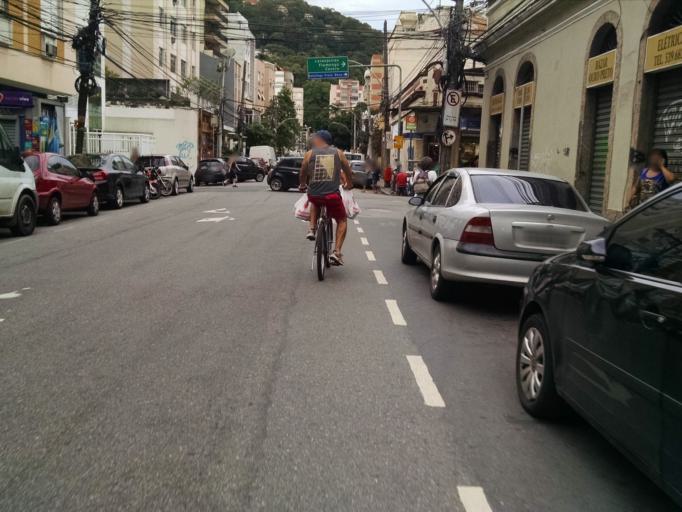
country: BR
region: Rio de Janeiro
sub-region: Rio De Janeiro
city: Rio de Janeiro
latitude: -22.9464
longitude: -43.1857
